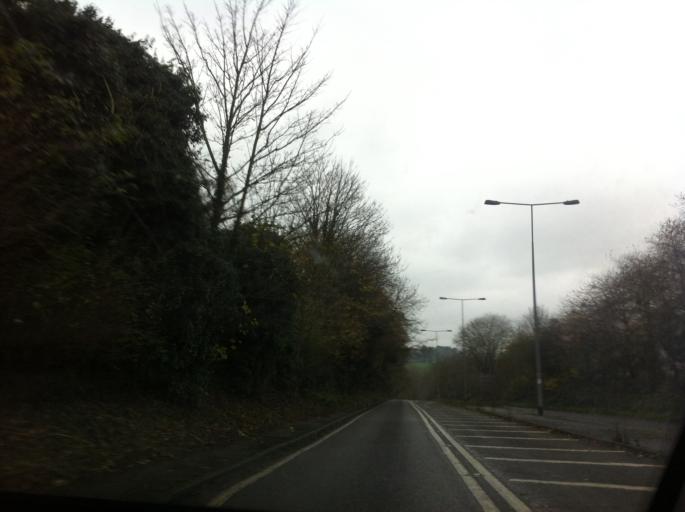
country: GB
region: England
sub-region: Northamptonshire
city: Earls Barton
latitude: 52.2628
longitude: -0.7116
